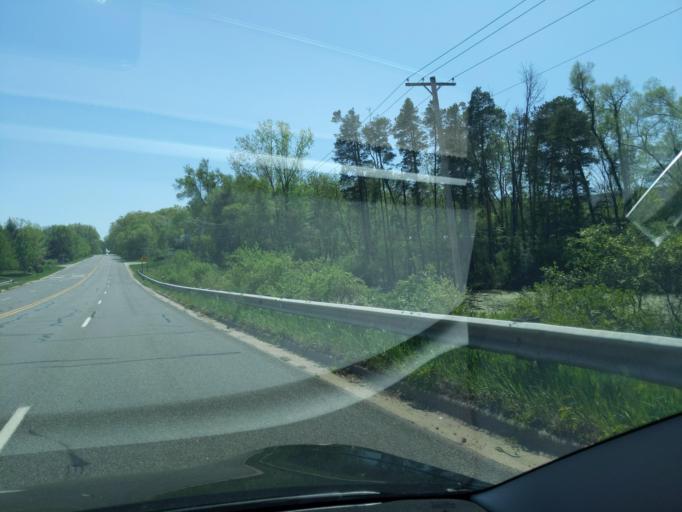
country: US
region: Michigan
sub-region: Kent County
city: Forest Hills
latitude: 42.9591
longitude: -85.5402
